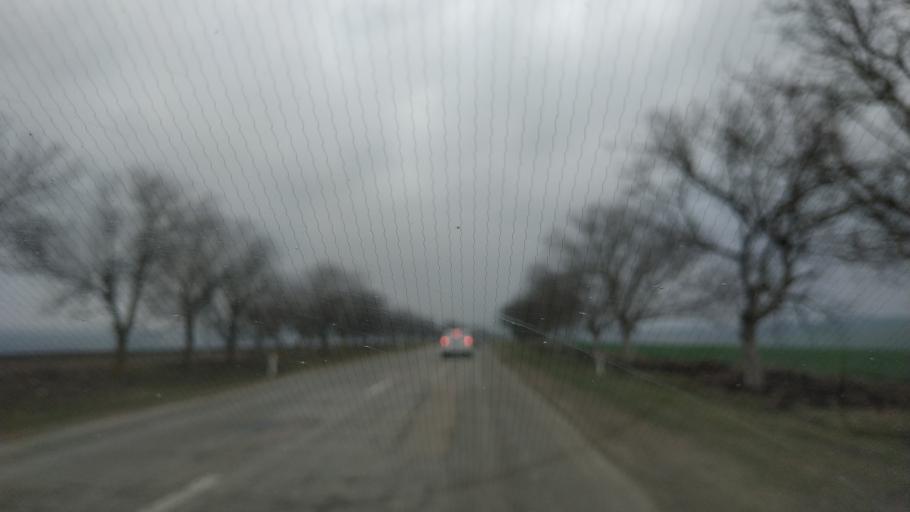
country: MD
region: Gagauzia
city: Comrat
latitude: 46.2577
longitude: 28.7521
